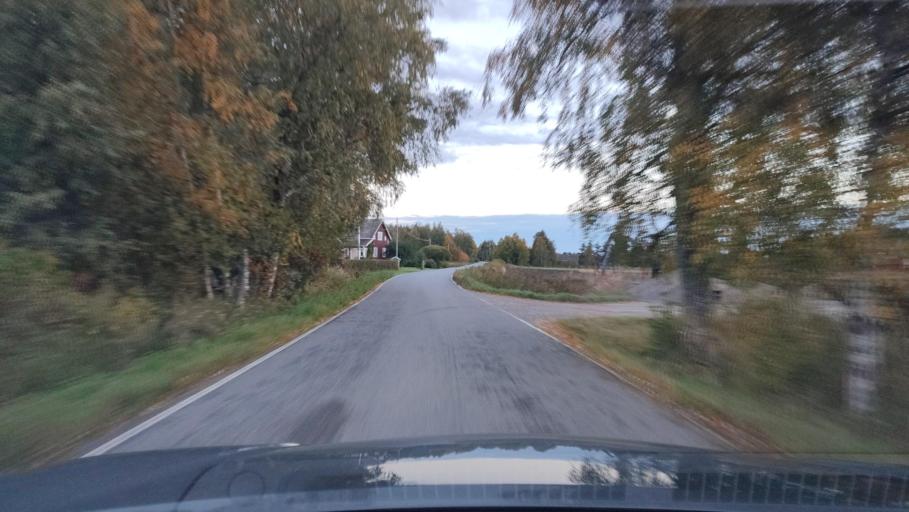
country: FI
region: Ostrobothnia
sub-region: Sydosterbotten
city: Kristinestad
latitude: 62.2698
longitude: 21.5247
